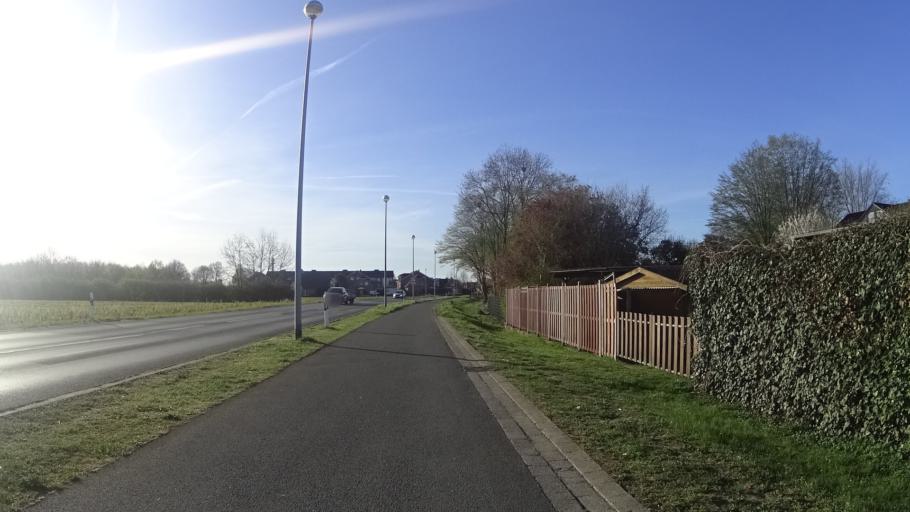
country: DE
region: North Rhine-Westphalia
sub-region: Regierungsbezirk Munster
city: Greven
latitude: 52.1027
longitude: 7.5869
